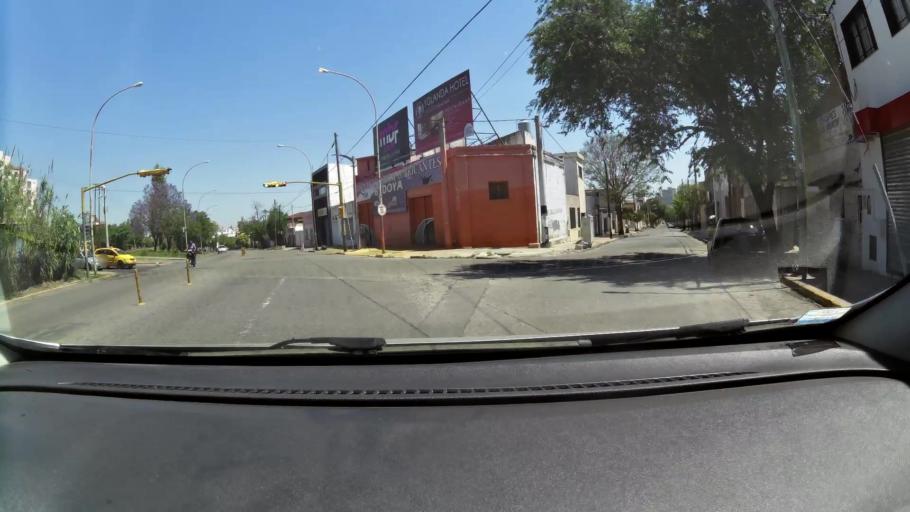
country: AR
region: Cordoba
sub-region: Departamento de Capital
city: Cordoba
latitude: -31.3955
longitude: -64.1937
